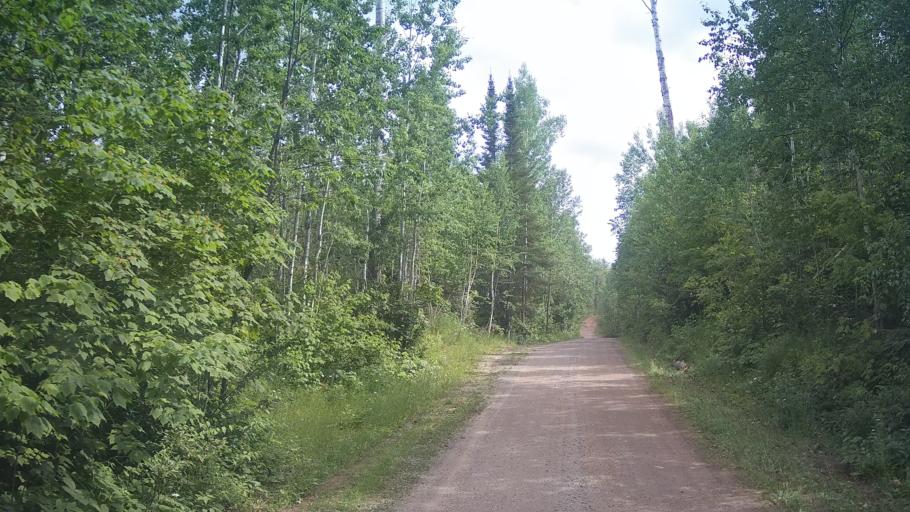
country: CA
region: Ontario
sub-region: Thunder Bay District
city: Thunder Bay
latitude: 48.6846
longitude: -88.6645
